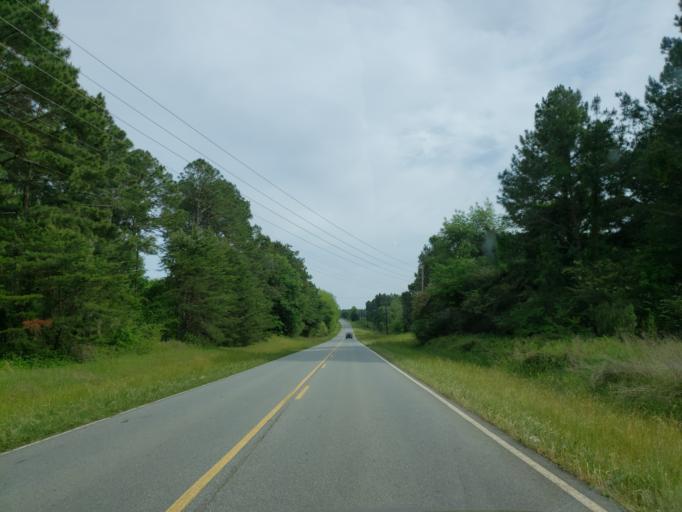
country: US
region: Georgia
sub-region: Dooly County
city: Vienna
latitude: 32.1769
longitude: -83.8922
